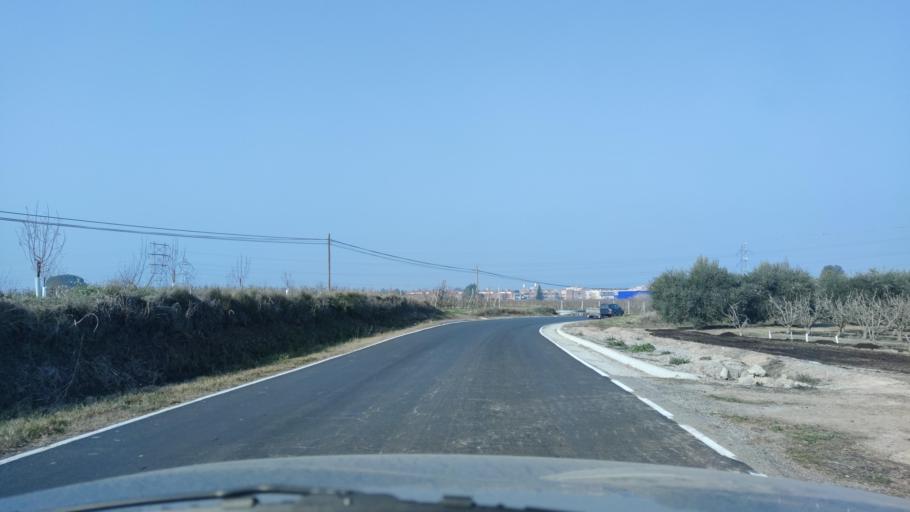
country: ES
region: Catalonia
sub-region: Provincia de Lleida
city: Alfes
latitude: 41.5676
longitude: 0.6107
